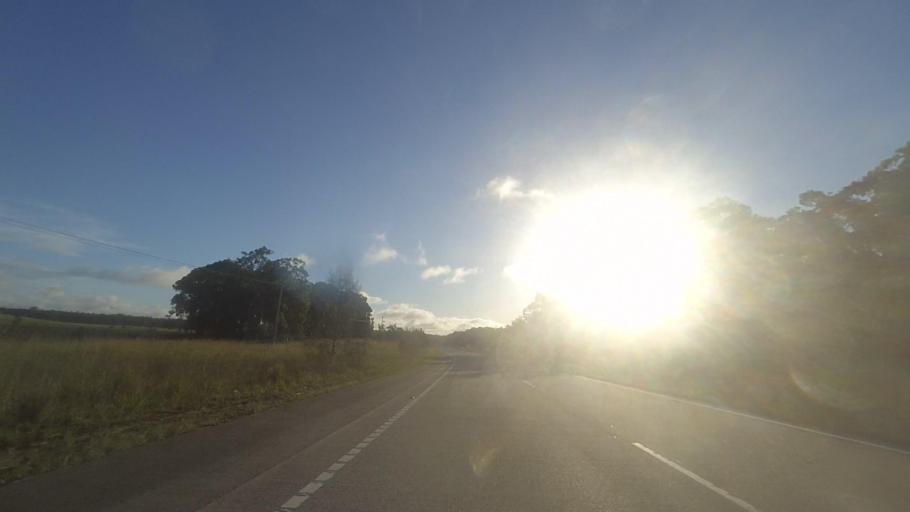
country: AU
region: New South Wales
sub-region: Great Lakes
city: Hawks Nest
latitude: -32.5385
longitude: 152.1702
